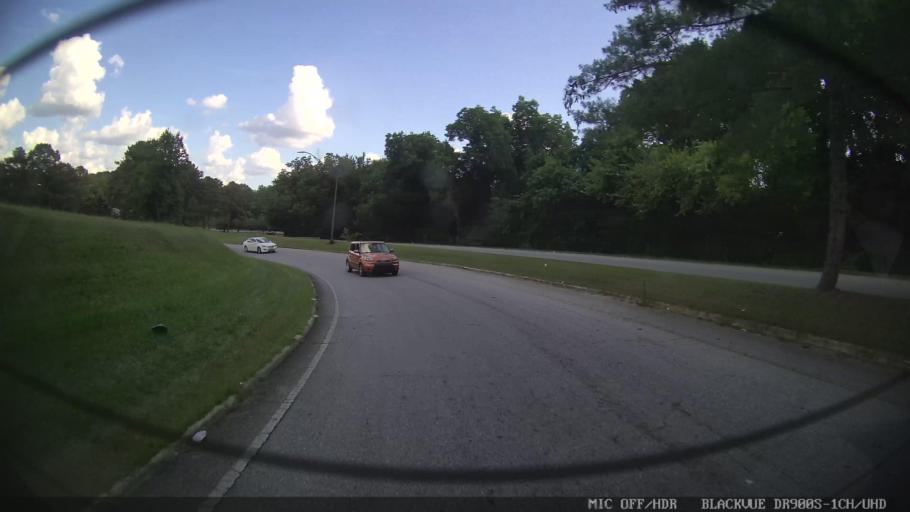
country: US
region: Georgia
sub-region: Floyd County
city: Rome
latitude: 34.2382
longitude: -85.1651
